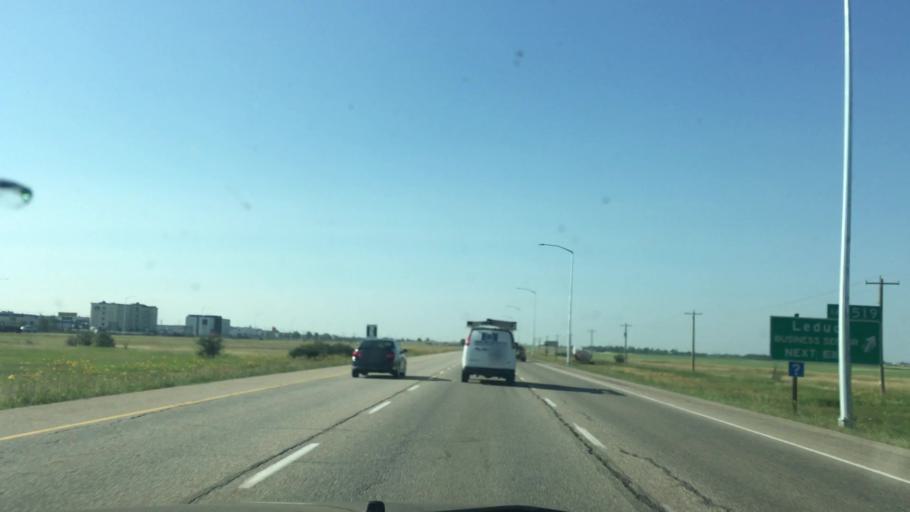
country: CA
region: Alberta
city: Leduc
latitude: 53.2979
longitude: -113.5499
